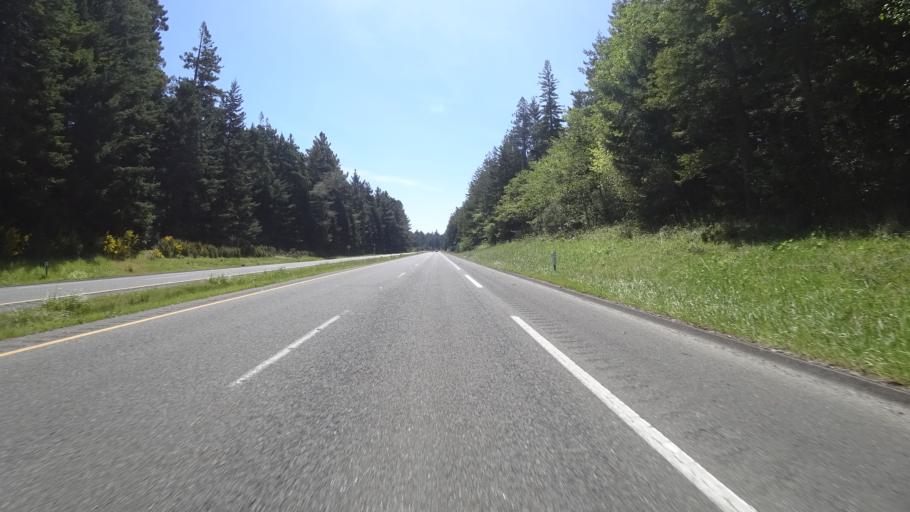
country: US
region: California
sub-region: Humboldt County
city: Westhaven-Moonstone
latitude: 41.0799
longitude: -124.1443
